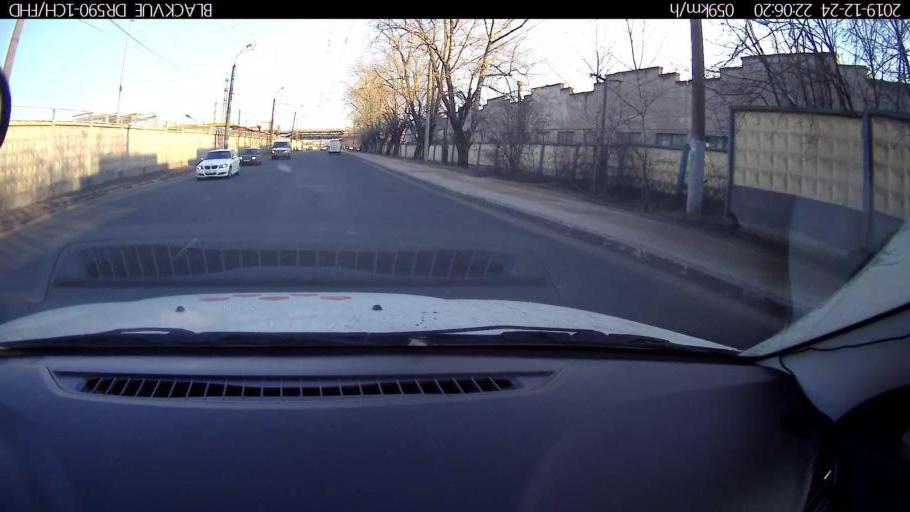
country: RU
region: Nizjnij Novgorod
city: Nizhniy Novgorod
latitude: 56.2419
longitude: 43.8990
